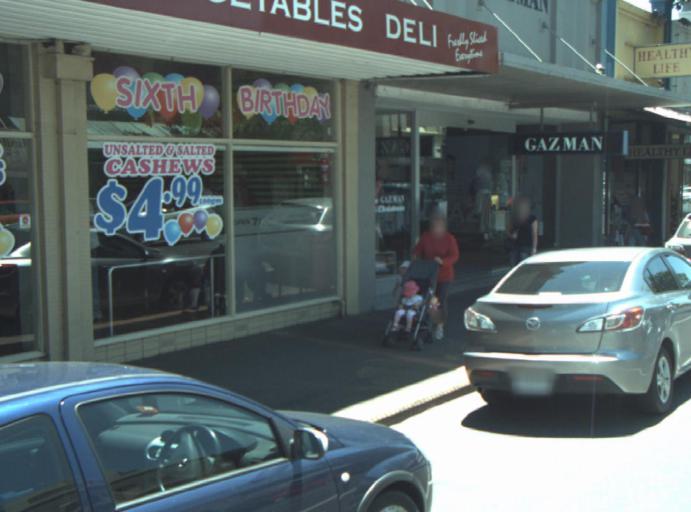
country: AU
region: Victoria
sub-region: Greater Geelong
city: Geelong West
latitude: -38.1420
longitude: 144.3480
